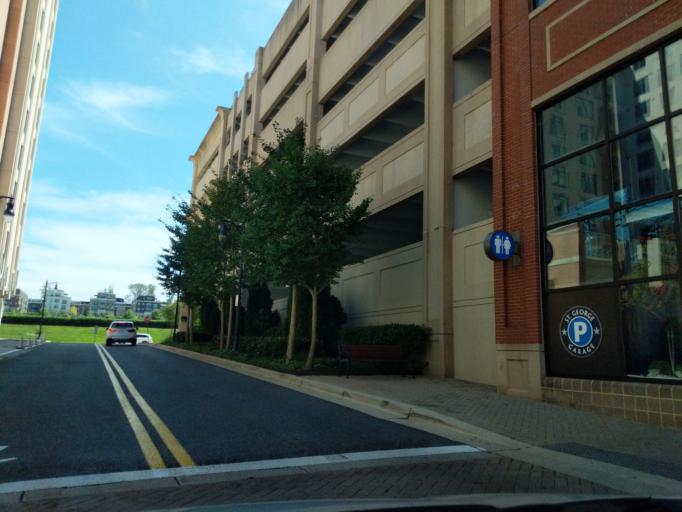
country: US
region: Maryland
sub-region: Prince George's County
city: Forest Heights
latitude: 38.7833
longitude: -77.0147
